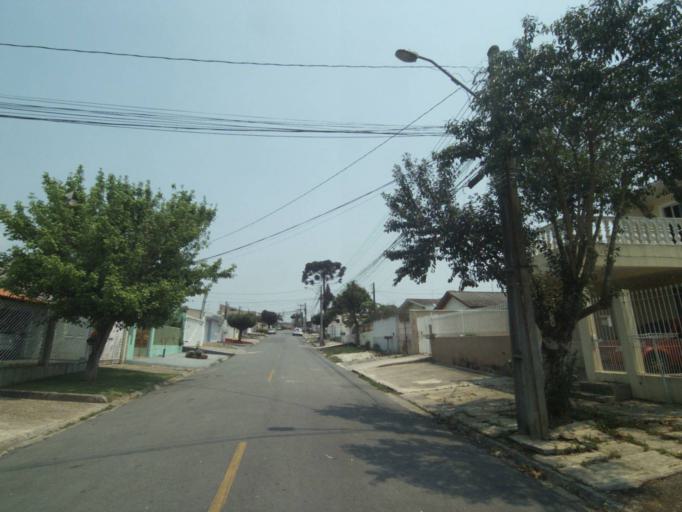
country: BR
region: Parana
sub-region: Sao Jose Dos Pinhais
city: Sao Jose dos Pinhais
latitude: -25.5261
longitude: -49.2450
